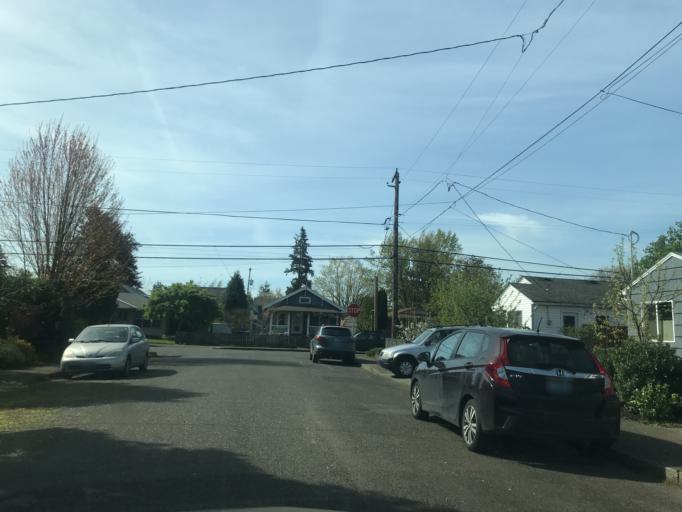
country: US
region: Oregon
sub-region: Multnomah County
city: Lents
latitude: 45.4943
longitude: -122.5902
